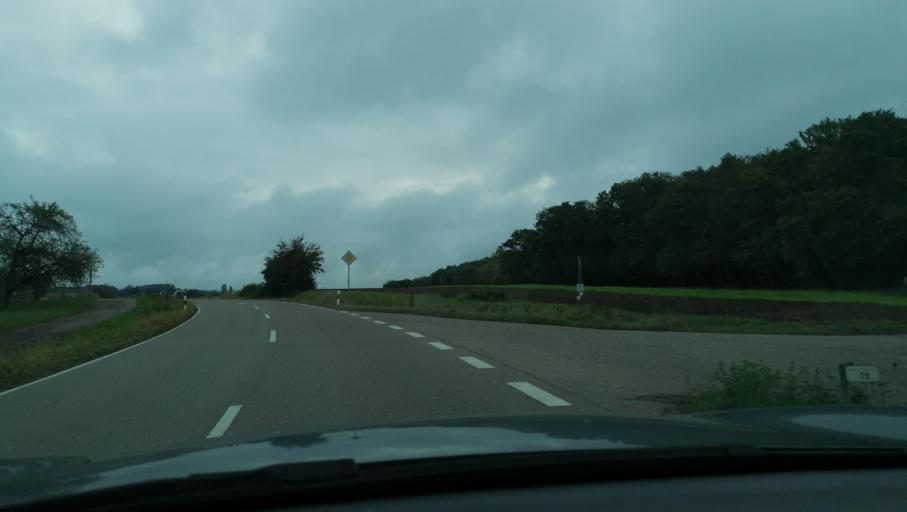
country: DE
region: Baden-Wuerttemberg
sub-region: Regierungsbezirk Stuttgart
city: Winterbach
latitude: 48.8433
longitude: 9.4767
